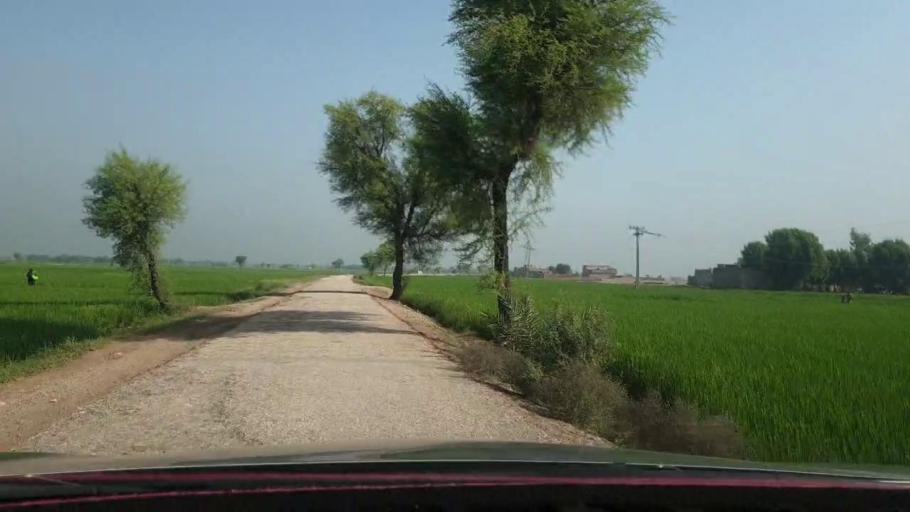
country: PK
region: Sindh
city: Nasirabad
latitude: 27.4826
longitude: 67.9256
